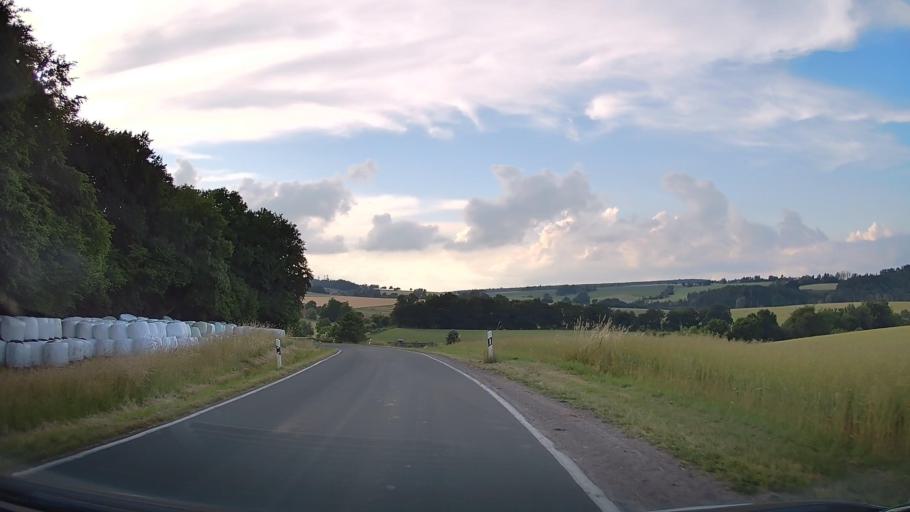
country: DE
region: North Rhine-Westphalia
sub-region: Regierungsbezirk Detmold
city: Lugde
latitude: 51.9568
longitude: 9.1881
